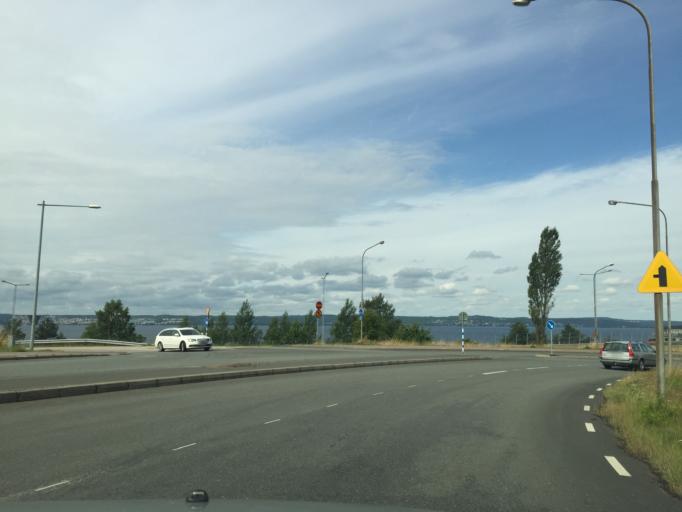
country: SE
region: Joenkoeping
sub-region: Jonkopings Kommun
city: Huskvarna
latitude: 57.8148
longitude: 14.2733
